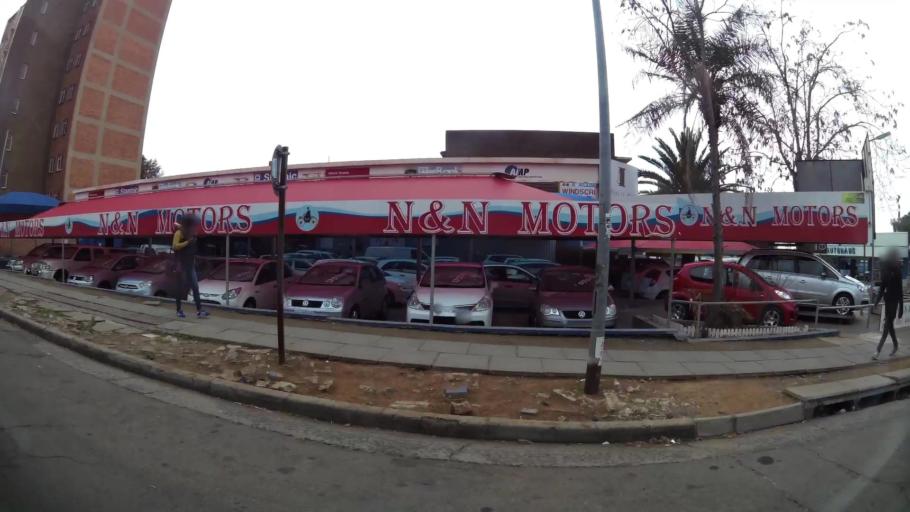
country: ZA
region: Orange Free State
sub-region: Mangaung Metropolitan Municipality
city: Bloemfontein
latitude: -29.1227
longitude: 26.2203
